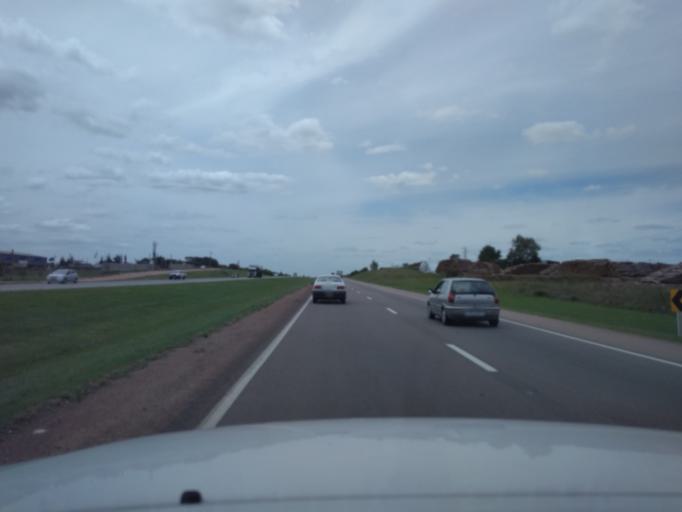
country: UY
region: Canelones
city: La Paz
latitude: -34.7451
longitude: -56.2525
